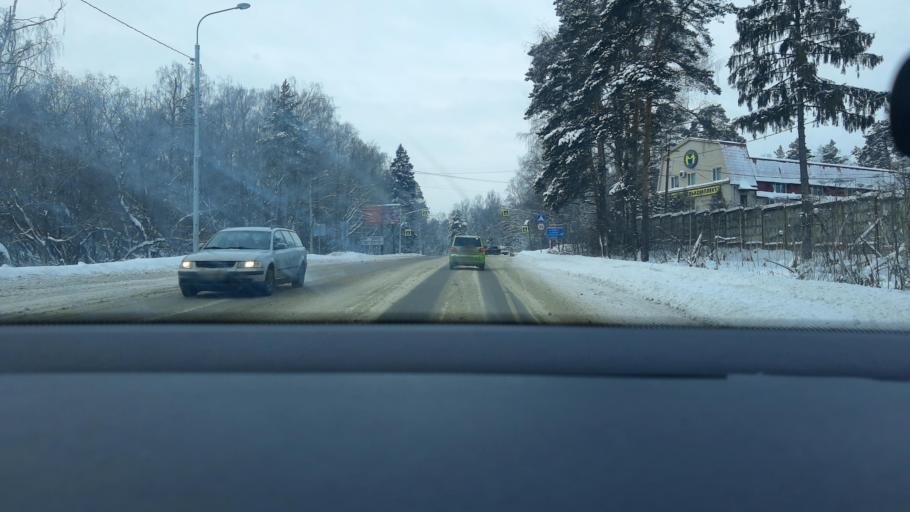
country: RU
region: Moskovskaya
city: Kostino
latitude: 56.0232
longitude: 37.9384
